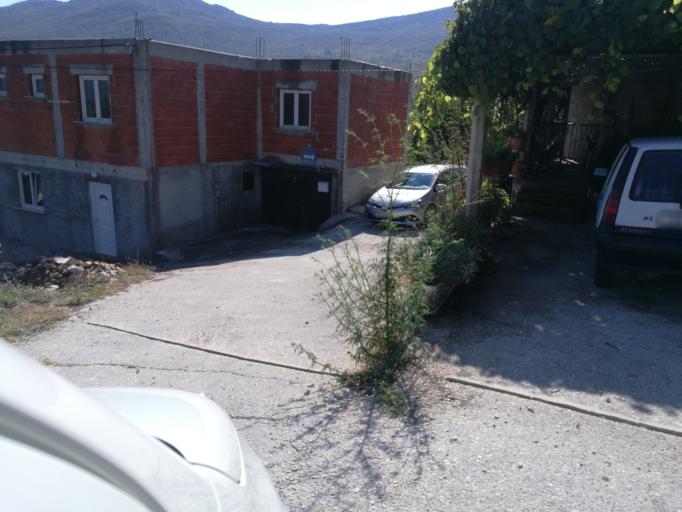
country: HR
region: Splitsko-Dalmatinska
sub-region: Grad Omis
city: Omis
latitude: 43.5166
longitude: 16.7290
